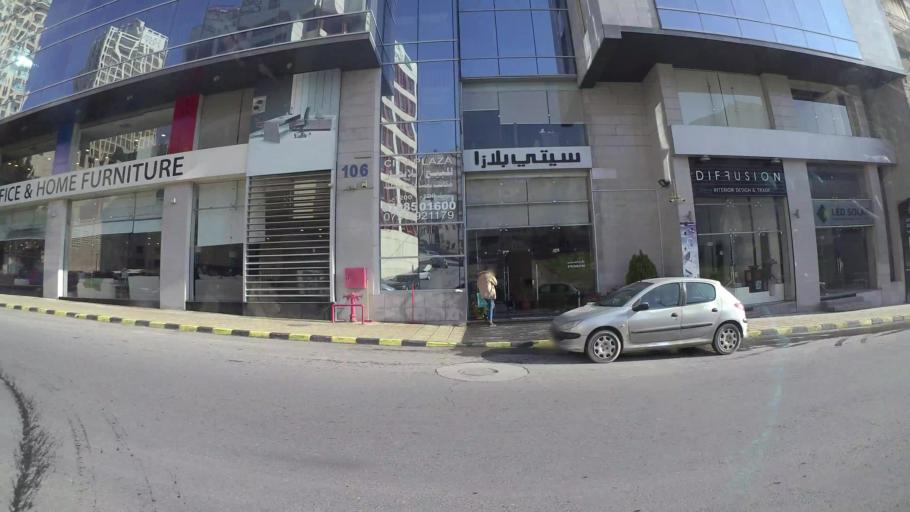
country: JO
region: Amman
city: Amman
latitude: 31.9571
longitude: 35.9114
